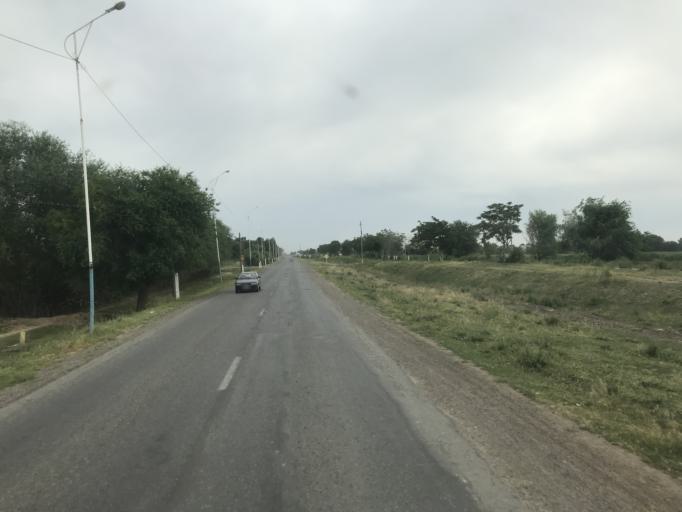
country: KZ
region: Ongtustik Qazaqstan
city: Asykata
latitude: 40.9406
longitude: 68.4141
